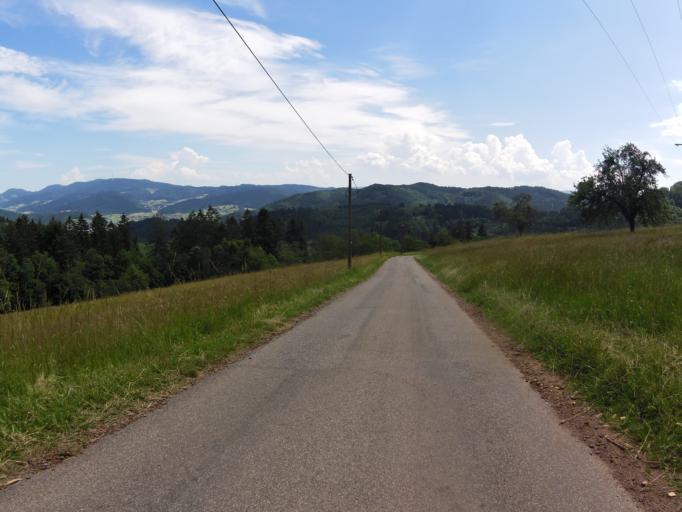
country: DE
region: Baden-Wuerttemberg
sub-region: Freiburg Region
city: Seelbach
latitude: 48.3332
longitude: 7.9829
